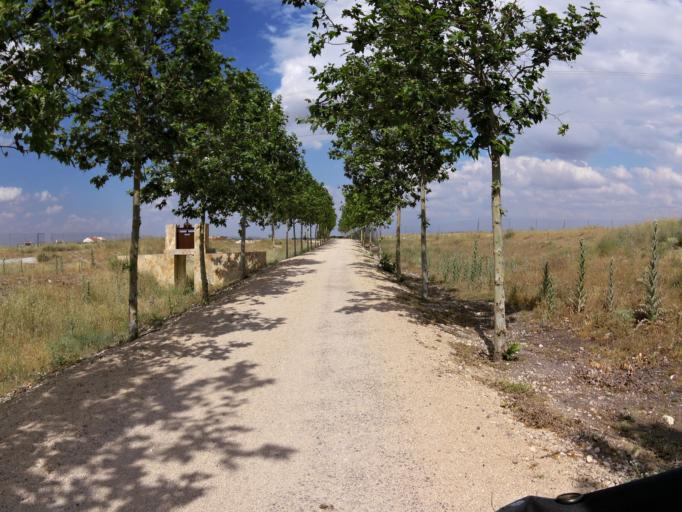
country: ES
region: Castille-La Mancha
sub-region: Provincia de Albacete
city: Albacete
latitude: 38.9641
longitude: -1.9559
